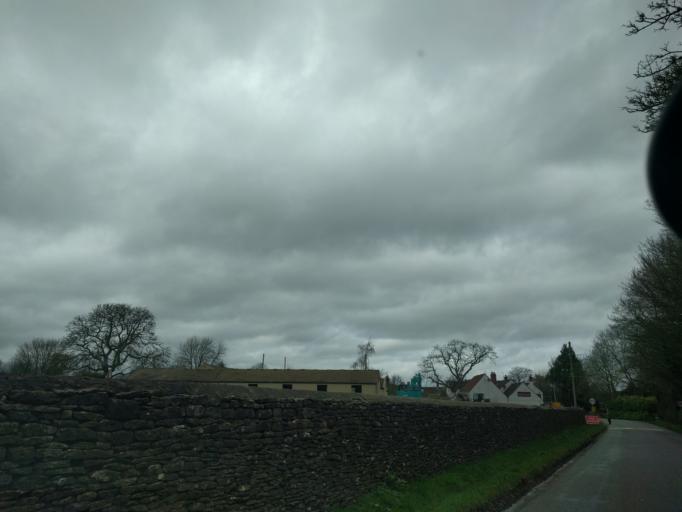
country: GB
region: England
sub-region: Wiltshire
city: Biddestone
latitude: 51.4593
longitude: -2.1944
